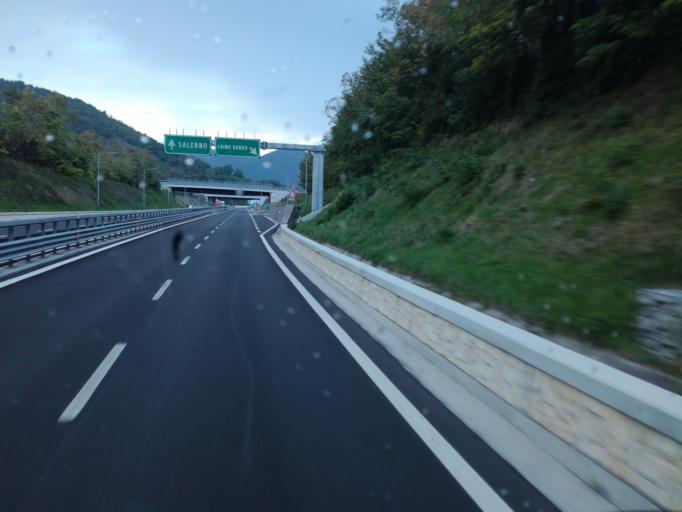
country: IT
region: Calabria
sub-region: Provincia di Cosenza
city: Laino Borgo
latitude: 39.9643
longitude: 15.9328
